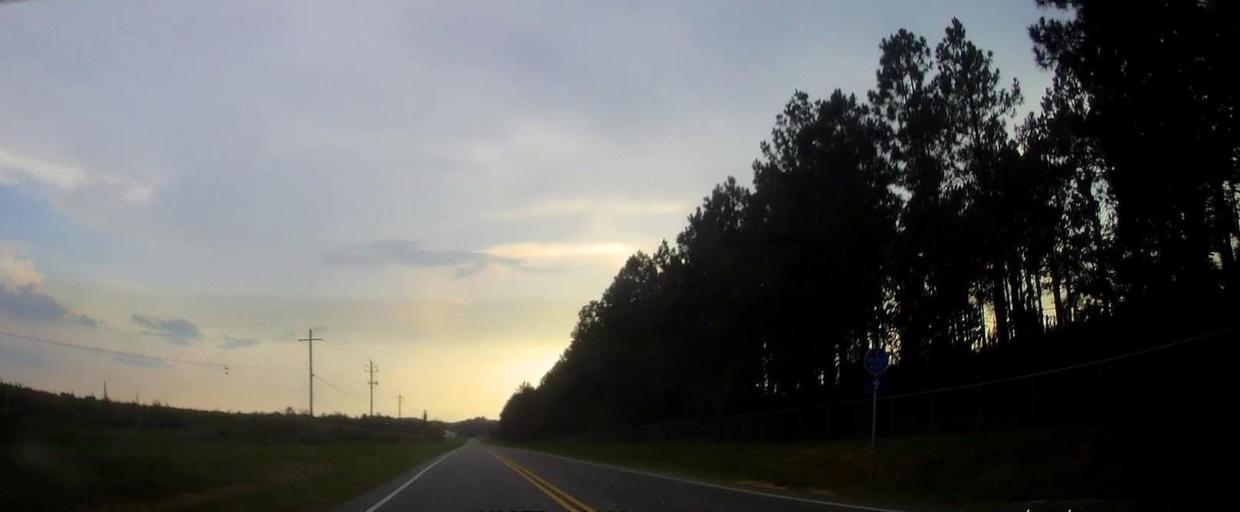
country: US
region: Georgia
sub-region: Laurens County
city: East Dublin
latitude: 32.5532
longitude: -82.8423
